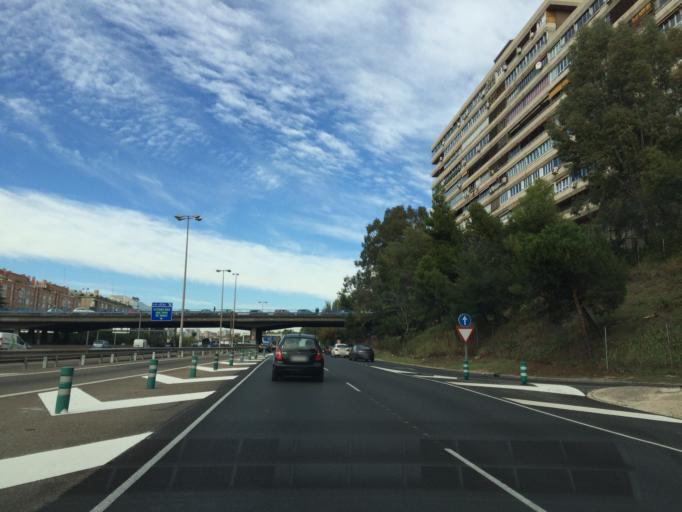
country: ES
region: Madrid
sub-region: Provincia de Madrid
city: Ciudad Lineal
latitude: 40.4518
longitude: -3.6626
